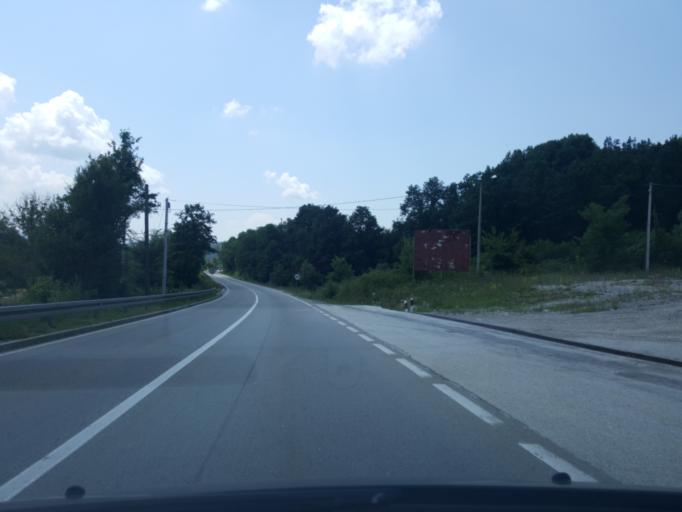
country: RS
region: Central Serbia
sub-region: Moravicki Okrug
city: Gornji Milanovac
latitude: 44.1007
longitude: 20.4812
